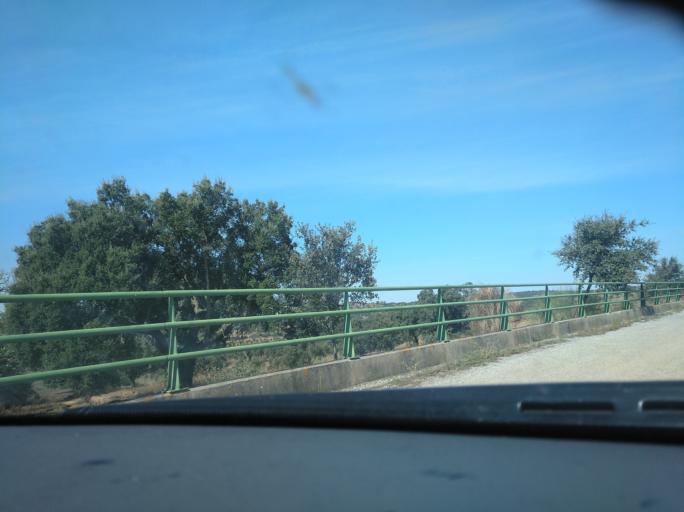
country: PT
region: Evora
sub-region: Montemor-O-Novo
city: Montemor-o-Novo
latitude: 38.6537
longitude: -8.0979
